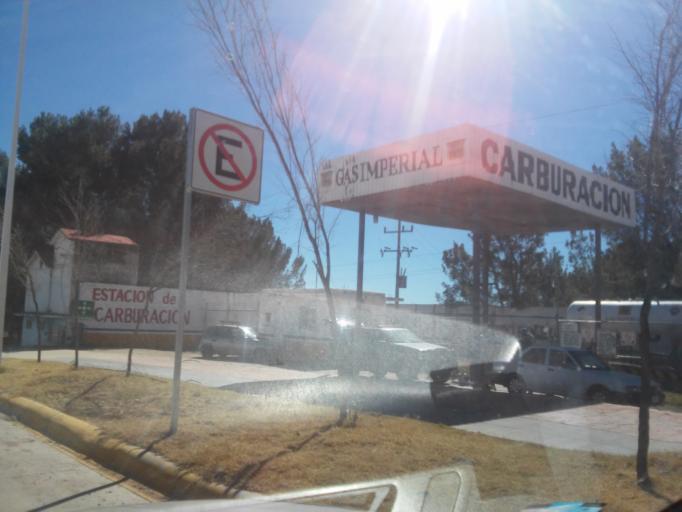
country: MX
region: Durango
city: Victoria de Durango
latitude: 23.9928
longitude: -104.7122
